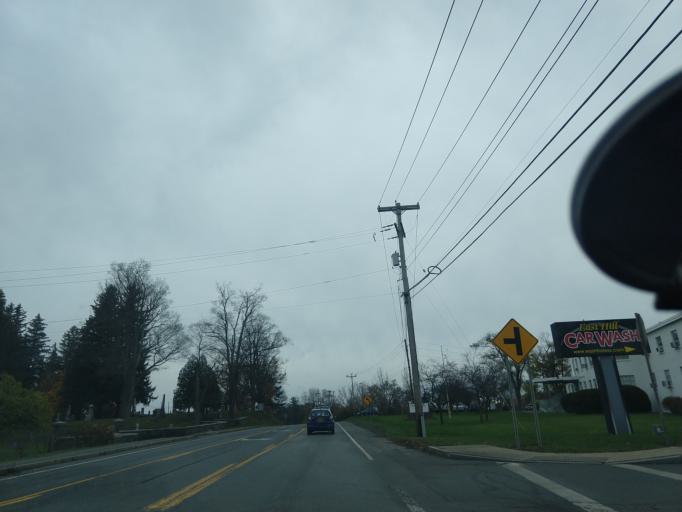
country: US
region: New York
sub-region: Tompkins County
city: East Ithaca
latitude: 42.4385
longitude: -76.4655
